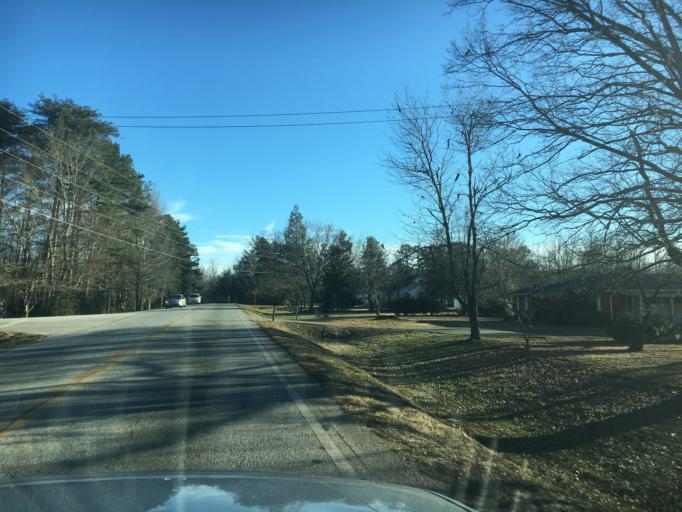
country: US
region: Georgia
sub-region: Habersham County
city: Demorest
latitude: 34.5552
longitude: -83.5735
